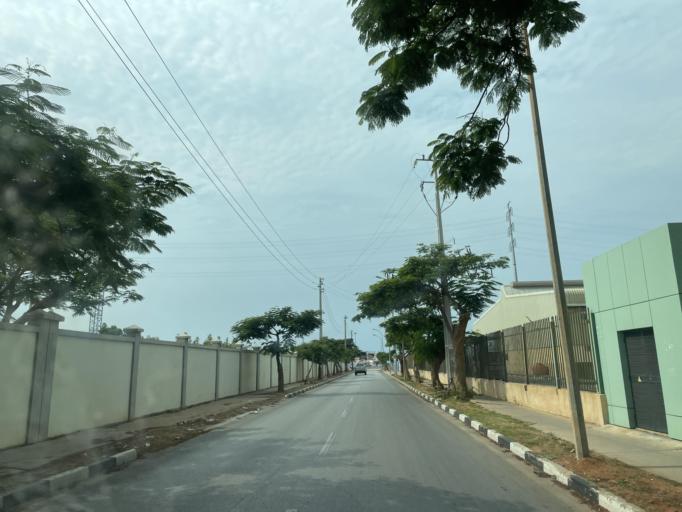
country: AO
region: Luanda
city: Luanda
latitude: -8.9141
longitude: 13.1984
